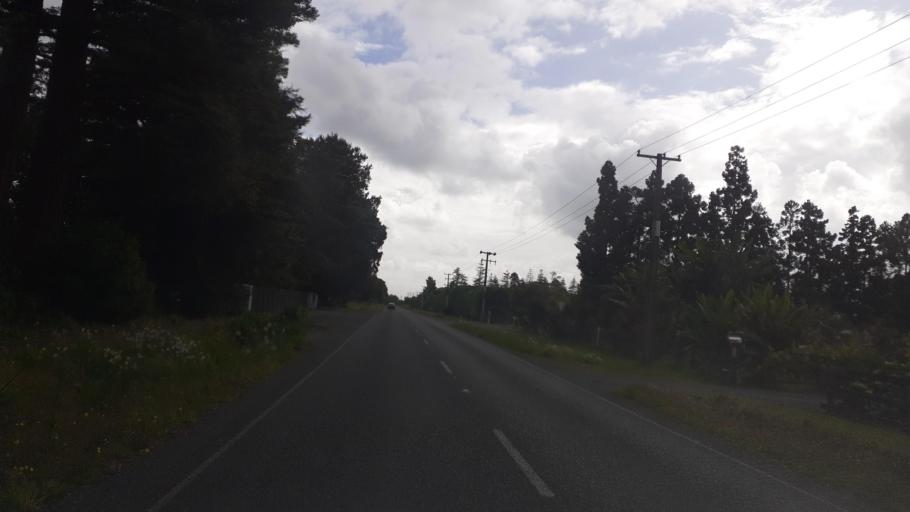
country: NZ
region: Northland
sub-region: Far North District
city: Kerikeri
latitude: -35.2254
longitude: 173.9710
